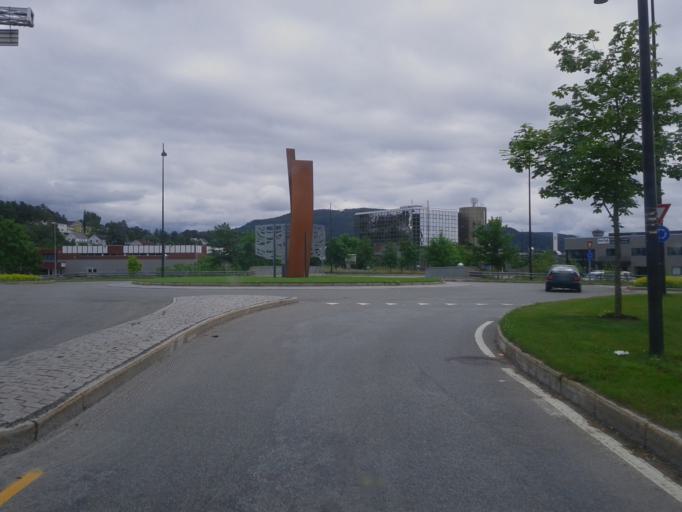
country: NO
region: Nord-Trondelag
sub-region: Steinkjer
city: Steinkjer
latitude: 64.0214
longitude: 11.4903
